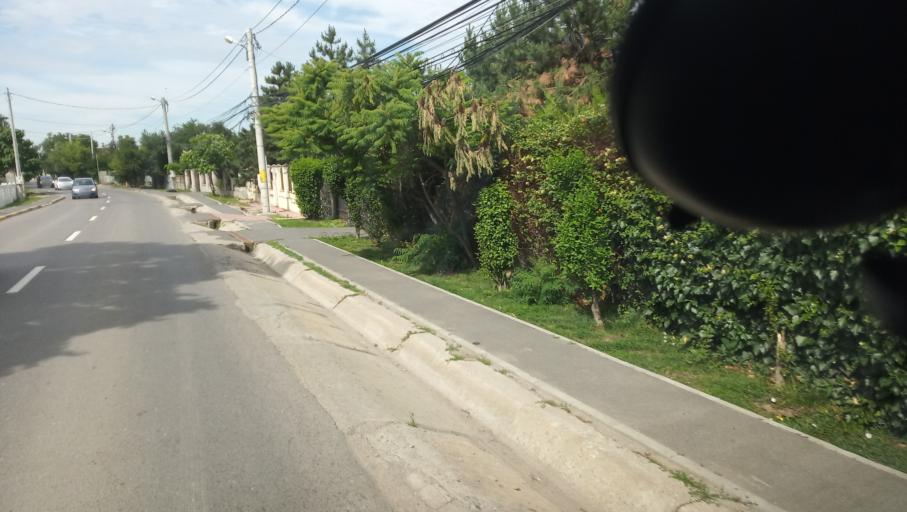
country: RO
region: Ilfov
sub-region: Comuna Otopeni
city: Otopeni
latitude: 44.5389
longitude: 26.0659
